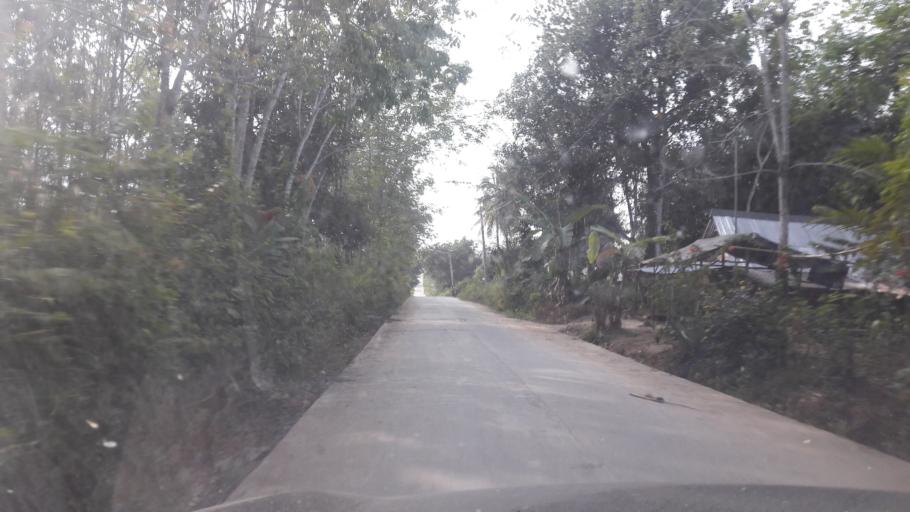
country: ID
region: South Sumatra
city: Gunungmenang
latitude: -3.2956
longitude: 103.9984
